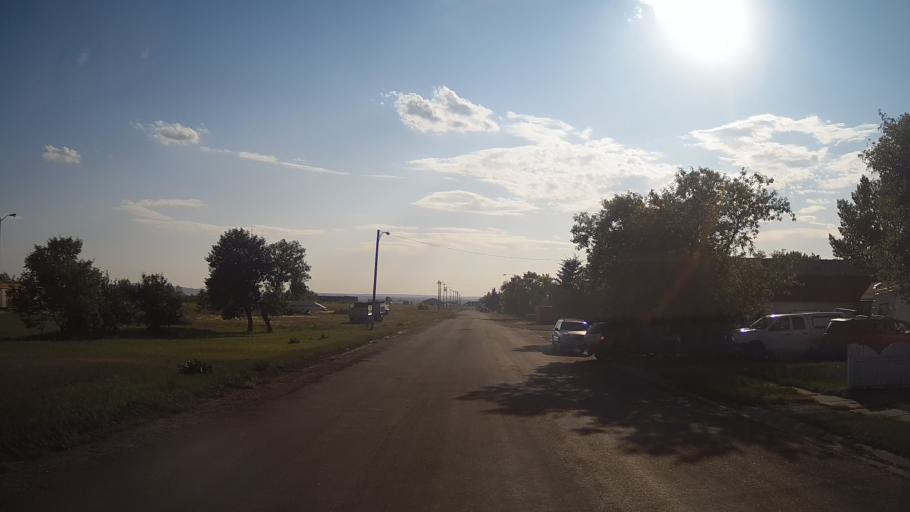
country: CA
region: Alberta
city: Hanna
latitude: 51.6416
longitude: -111.9261
